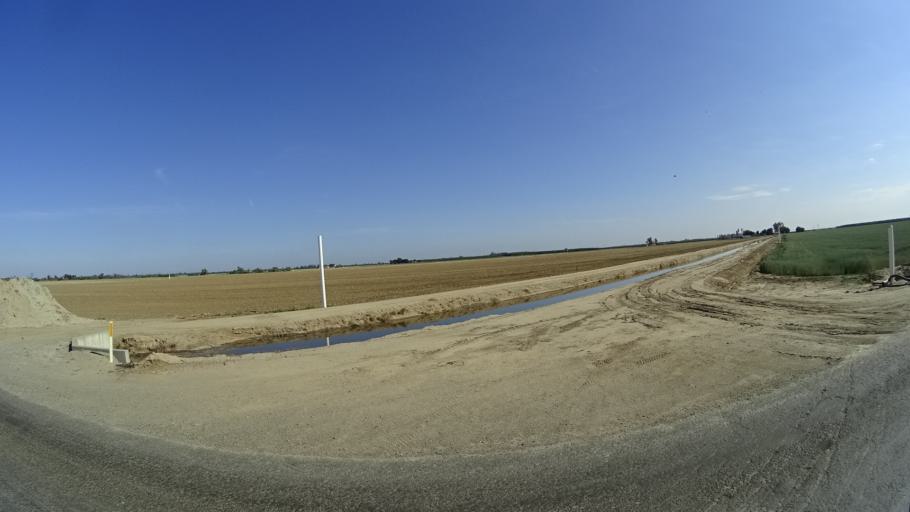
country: US
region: California
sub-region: Kings County
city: Armona
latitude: 36.2257
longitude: -119.7152
